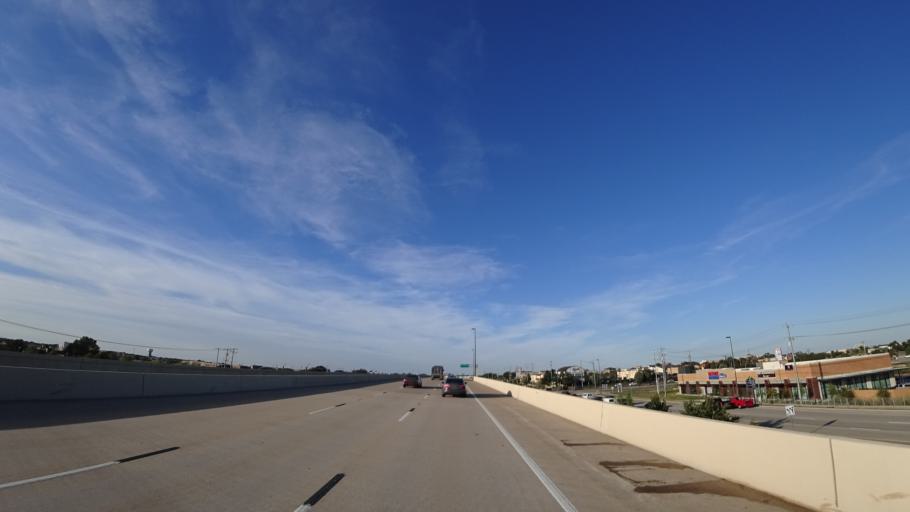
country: US
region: Texas
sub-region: Williamson County
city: Cedar Park
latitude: 30.5236
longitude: -97.8158
